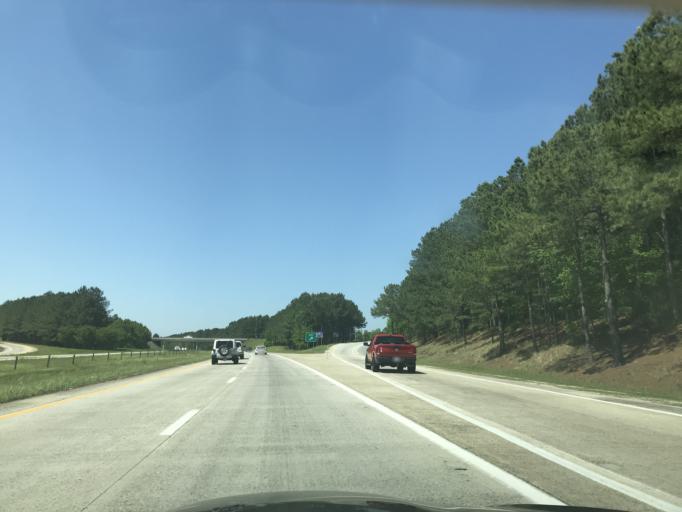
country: US
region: North Carolina
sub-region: Johnston County
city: Benson
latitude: 35.5132
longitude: -78.5562
